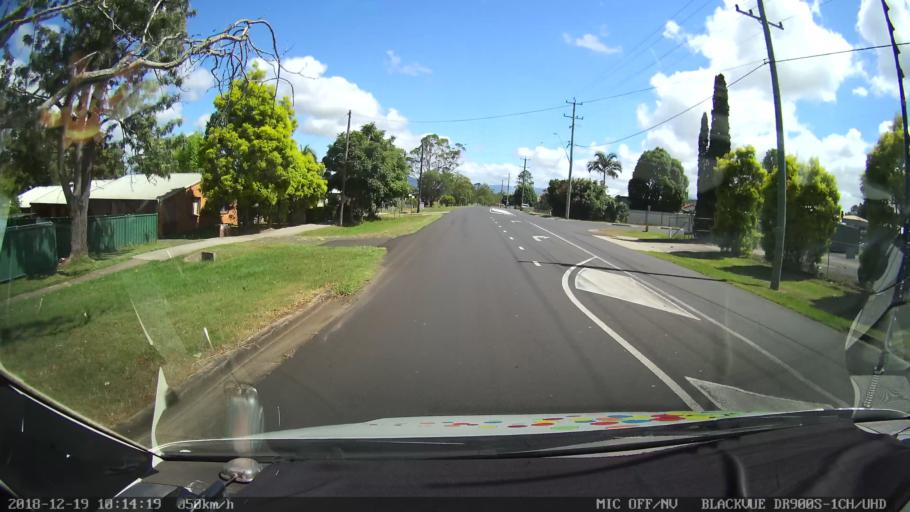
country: AU
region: New South Wales
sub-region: Kyogle
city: Kyogle
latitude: -28.6154
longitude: 153.0090
